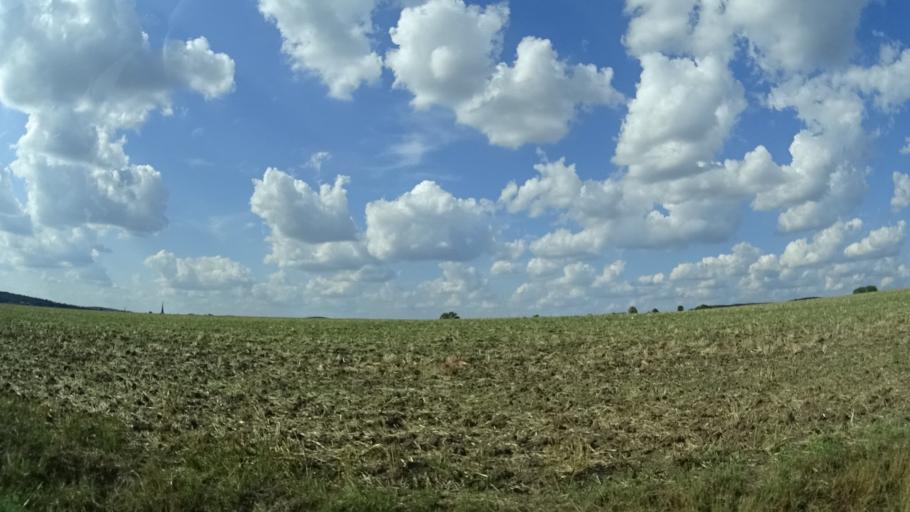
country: DE
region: Bavaria
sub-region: Regierungsbezirk Unterfranken
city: Trappstadt
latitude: 50.2861
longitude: 10.5737
